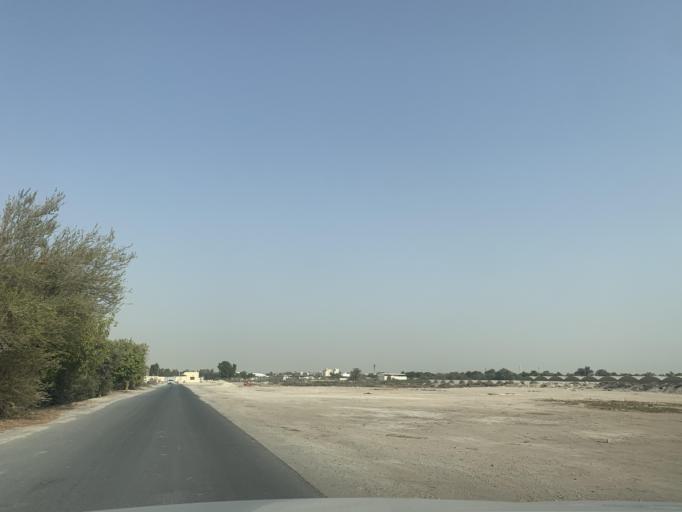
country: BH
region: Central Governorate
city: Madinat Hamad
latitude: 26.1571
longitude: 50.4887
